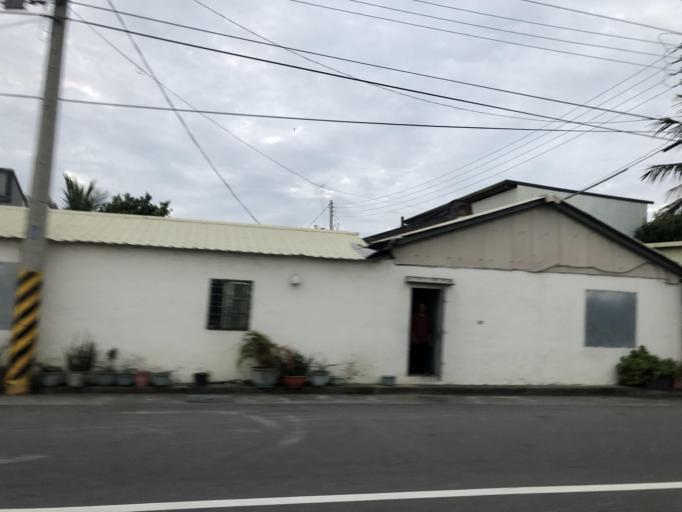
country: TW
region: Taiwan
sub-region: Tainan
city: Tainan
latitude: 23.0234
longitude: 120.2987
